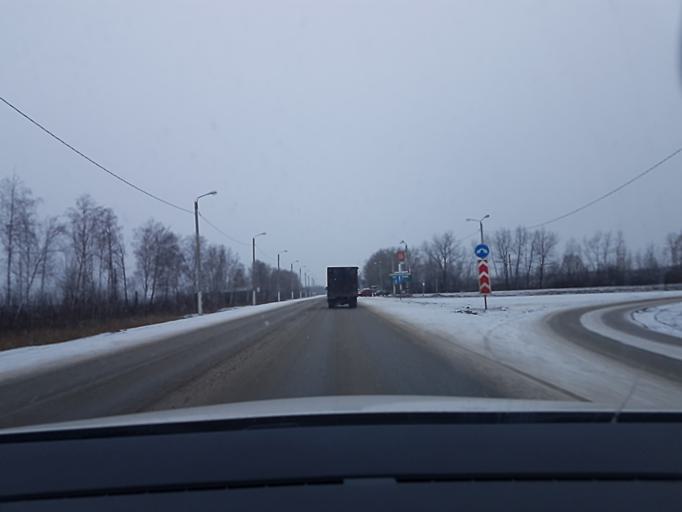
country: RU
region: Tambov
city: Pervomayskiy
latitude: 53.2448
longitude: 40.2548
